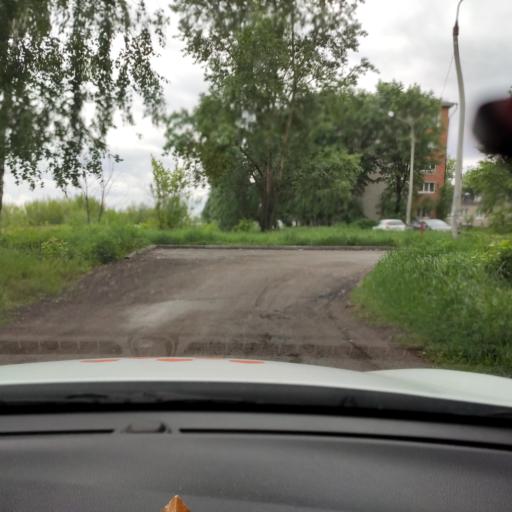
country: RU
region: Tatarstan
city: Staroye Arakchino
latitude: 55.8786
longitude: 49.0210
